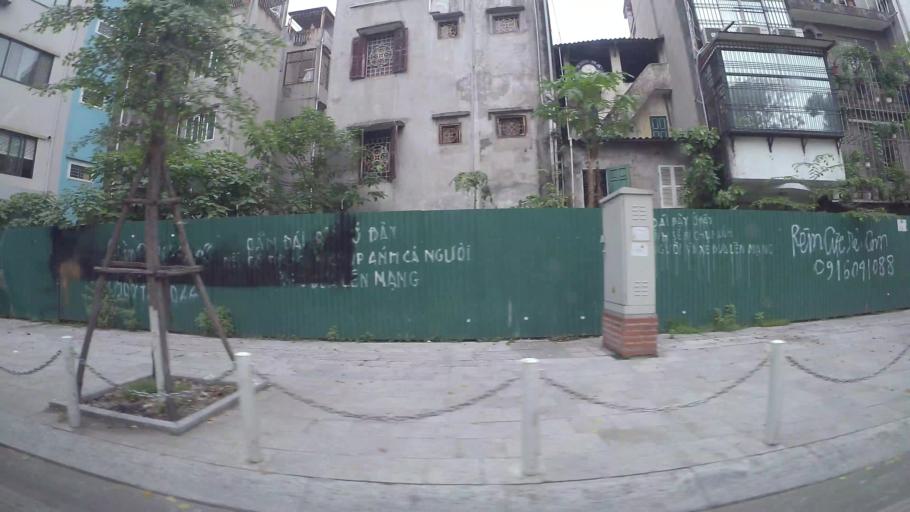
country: VN
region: Ha Noi
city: Hai BaTrung
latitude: 21.0088
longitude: 105.8461
